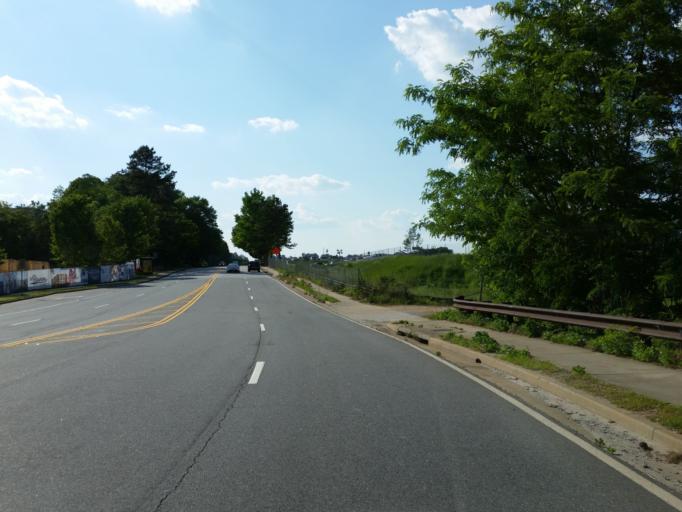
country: US
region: Georgia
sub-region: Cobb County
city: Vinings
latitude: 33.8948
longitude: -84.4672
